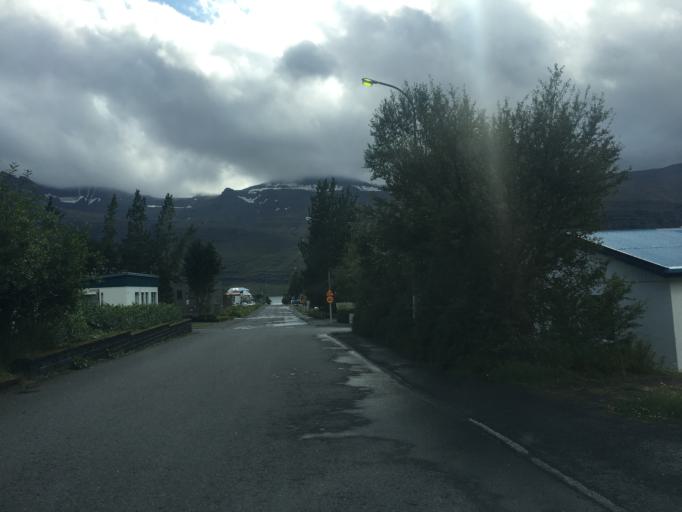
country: IS
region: East
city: Reydarfjoerdur
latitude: 65.0362
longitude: -14.2142
